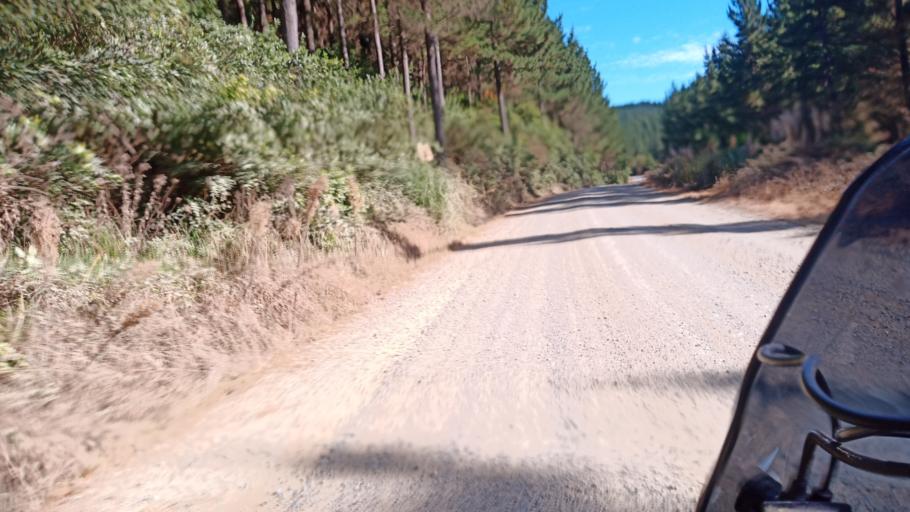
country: NZ
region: Hawke's Bay
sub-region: Wairoa District
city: Wairoa
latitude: -38.9234
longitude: 177.2056
